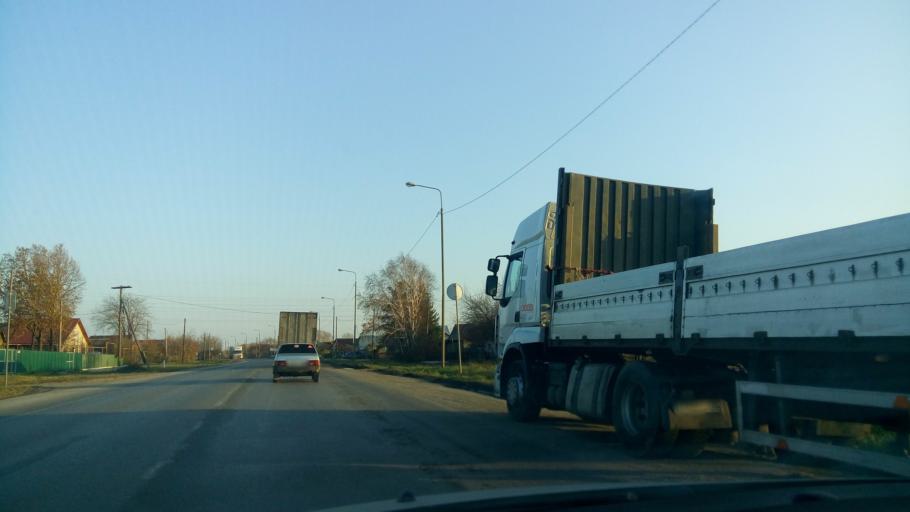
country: RU
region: Sverdlovsk
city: Bogdanovich
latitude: 56.7605
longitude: 62.0746
